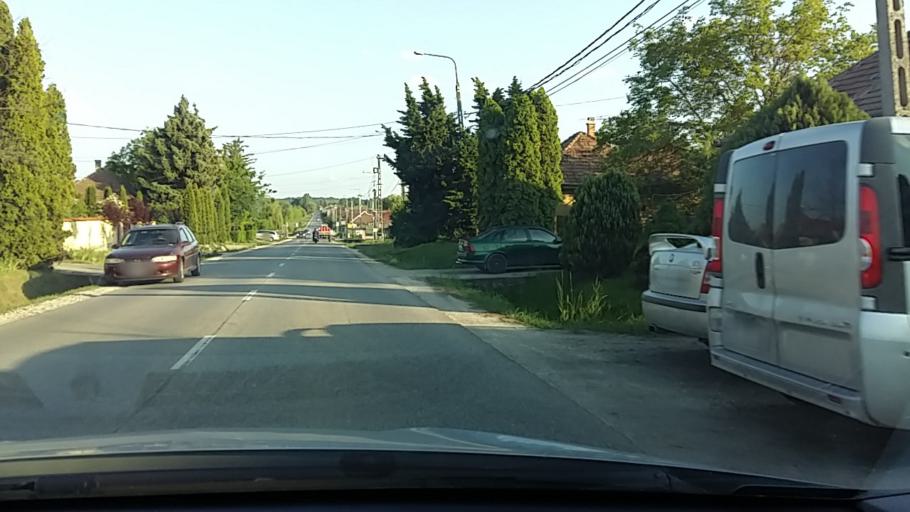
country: HU
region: Pest
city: Szod
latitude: 47.7213
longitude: 19.2296
